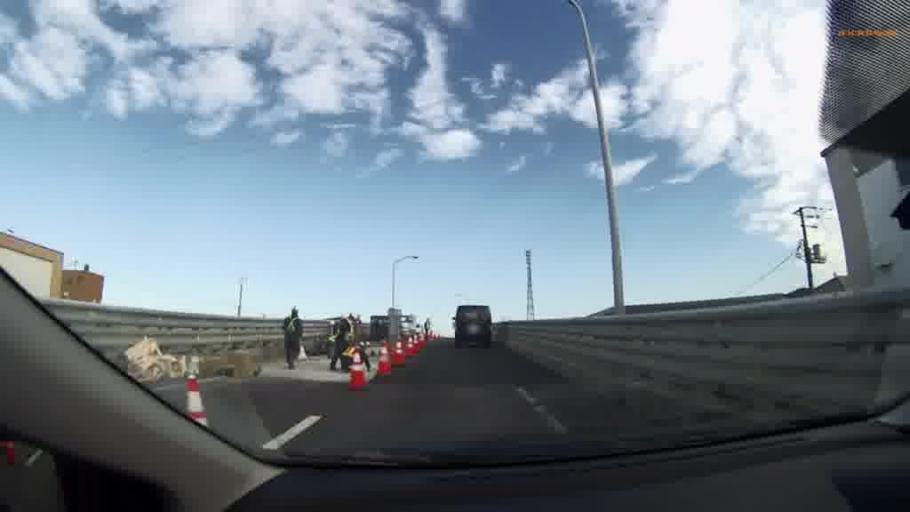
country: JP
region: Hokkaido
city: Kushiro
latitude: 42.9555
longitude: 144.0735
